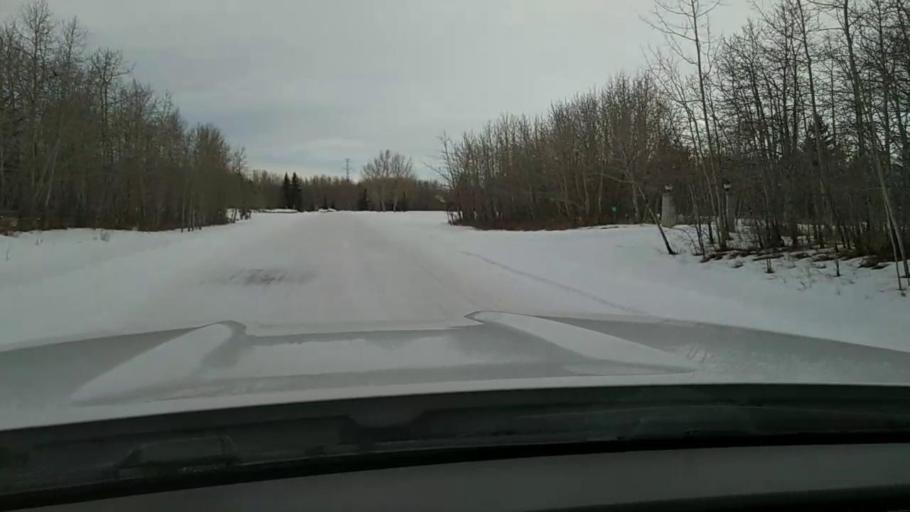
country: CA
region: Alberta
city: Calgary
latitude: 51.1847
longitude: -114.2533
